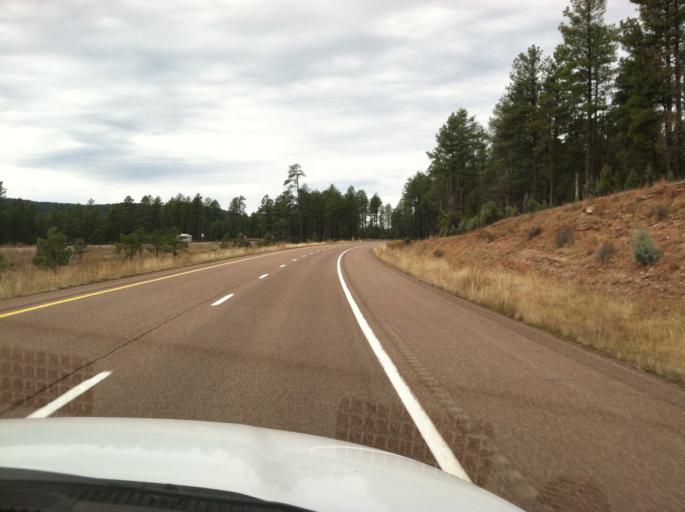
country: US
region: Arizona
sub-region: Gila County
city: Star Valley
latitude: 34.2943
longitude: -110.9767
